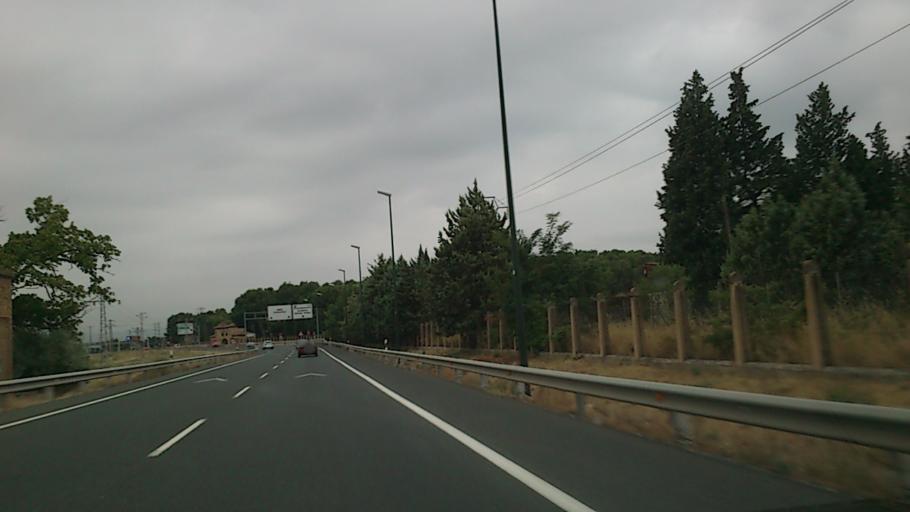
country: ES
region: Aragon
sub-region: Provincia de Zaragoza
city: Zaragoza
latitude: 41.7015
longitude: -0.8676
